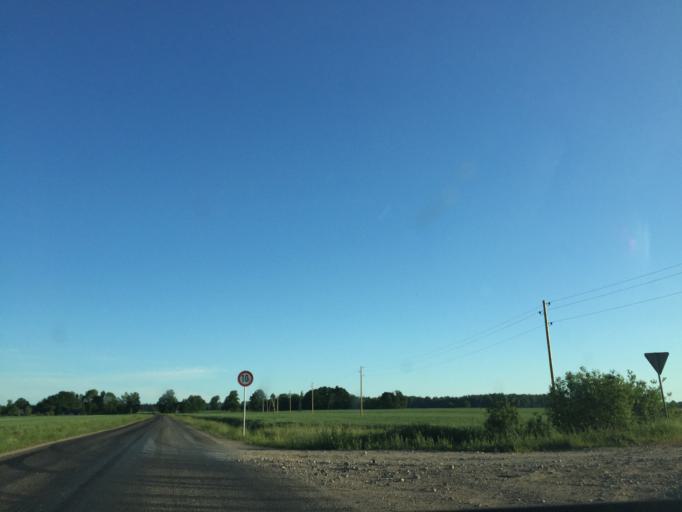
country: LV
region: Broceni
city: Broceni
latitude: 56.7486
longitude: 22.5144
